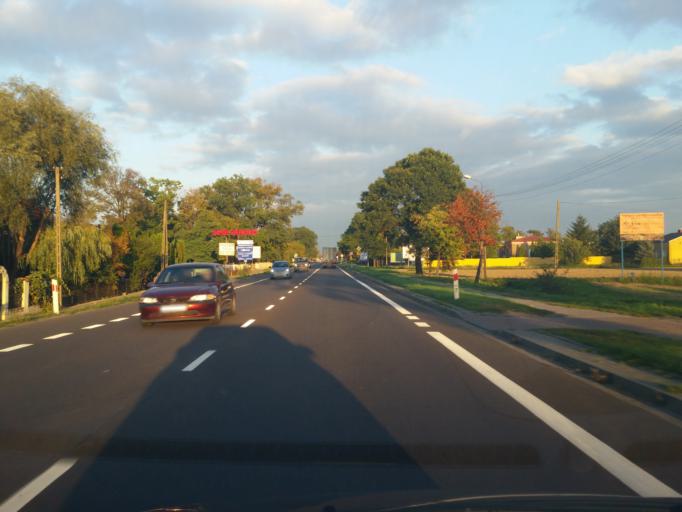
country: PL
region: Masovian Voivodeship
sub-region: Powiat warszawski zachodni
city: Ozarow Mazowiecki
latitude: 52.2113
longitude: 20.7600
